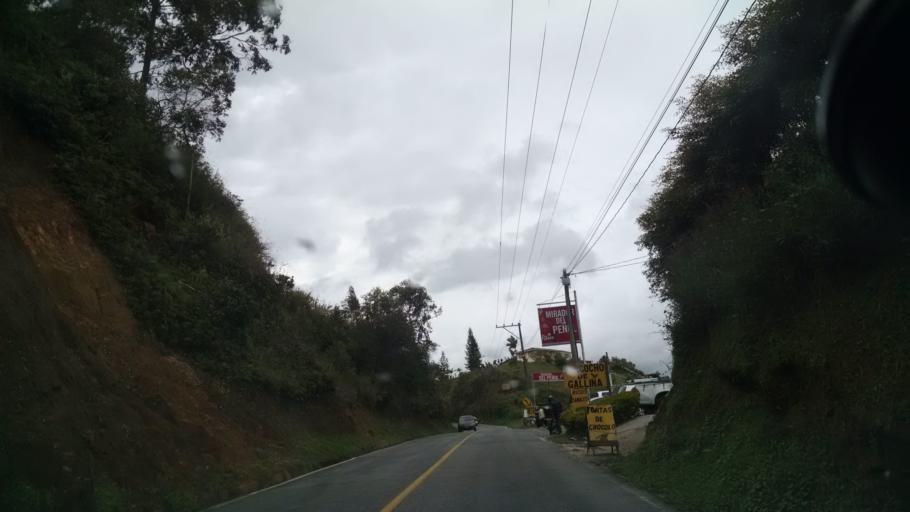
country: CO
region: Antioquia
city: Guatape
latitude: 6.2040
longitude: -75.2102
